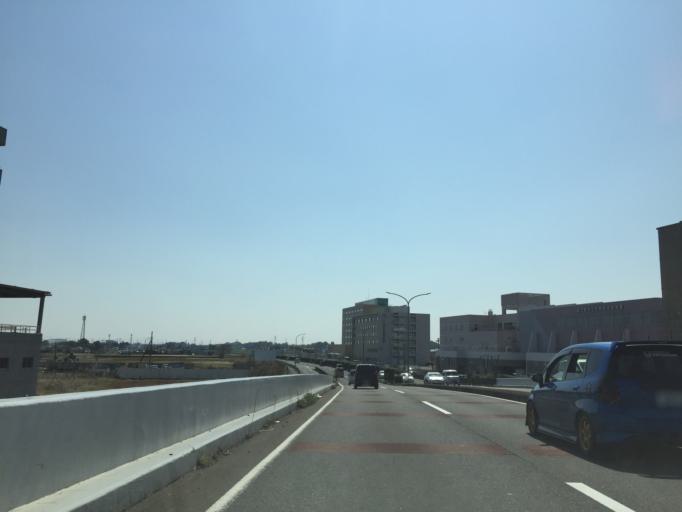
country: JP
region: Saitama
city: Oi
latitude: 35.8583
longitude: 139.5511
